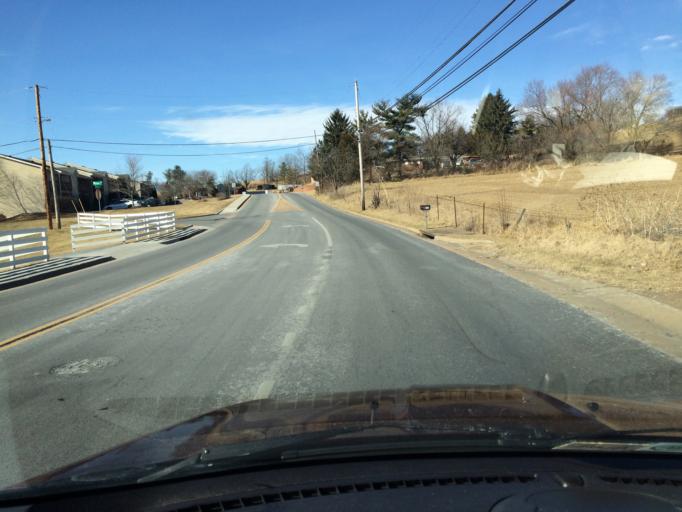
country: US
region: Virginia
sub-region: City of Harrisonburg
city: Harrisonburg
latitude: 38.4217
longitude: -78.8975
